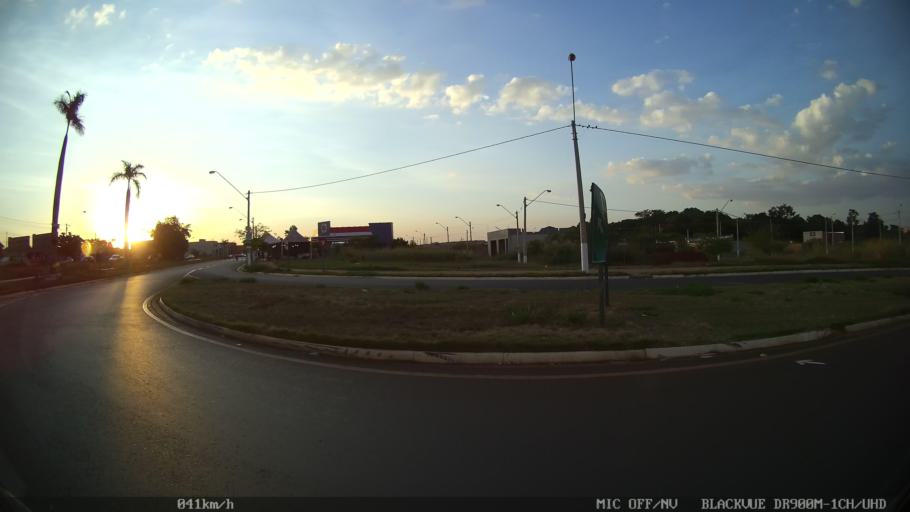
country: BR
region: Sao Paulo
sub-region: Ribeirao Preto
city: Ribeirao Preto
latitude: -21.1161
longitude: -47.8286
